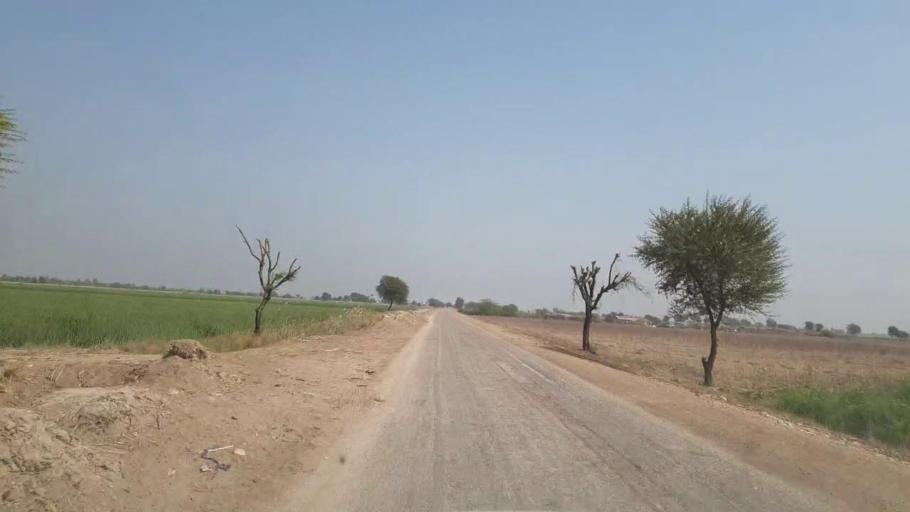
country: PK
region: Sindh
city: Mirpur Khas
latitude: 25.6459
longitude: 69.1604
